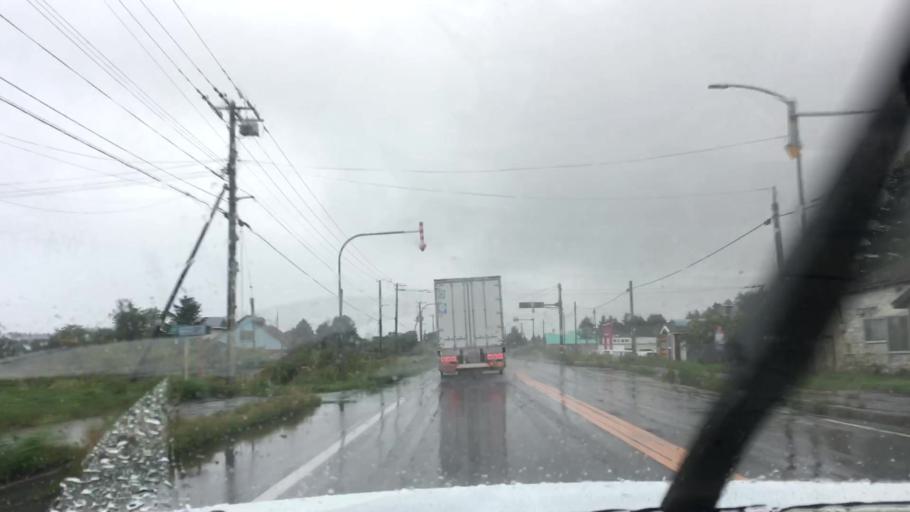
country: JP
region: Hokkaido
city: Niseko Town
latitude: 42.4774
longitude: 140.3481
